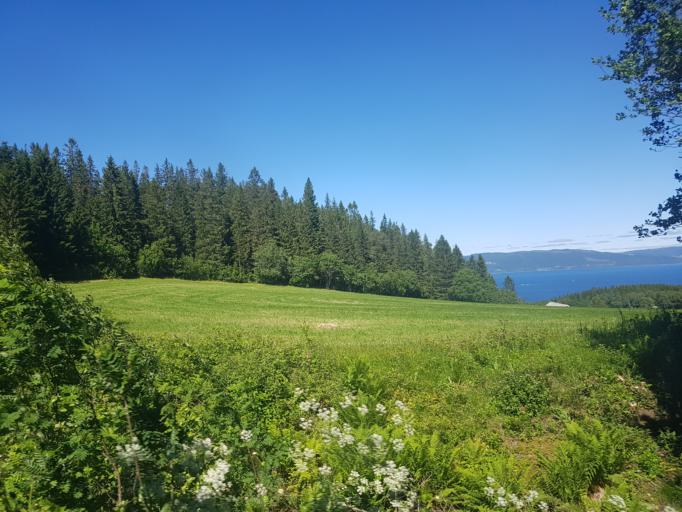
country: NO
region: Sor-Trondelag
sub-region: Skaun
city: Borsa
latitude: 63.4377
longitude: 10.1979
